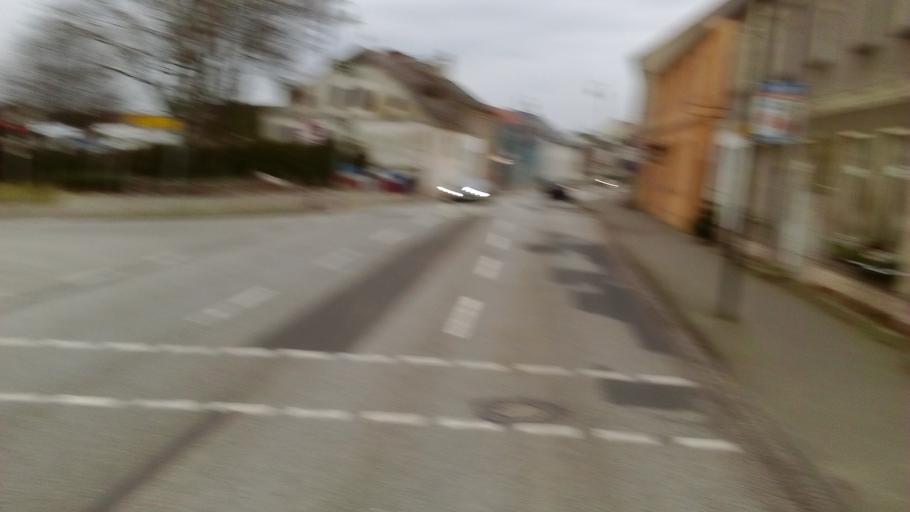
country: DE
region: Brandenburg
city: Brussow
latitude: 53.4537
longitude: 14.2103
